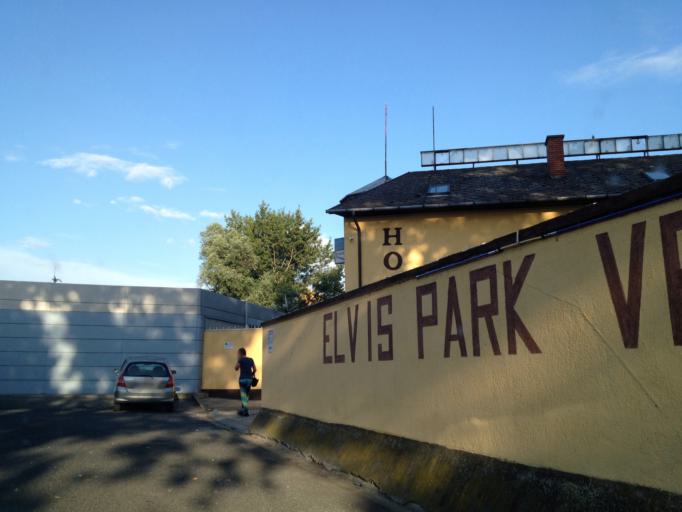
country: HU
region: Gyor-Moson-Sopron
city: Abda
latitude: 47.6836
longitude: 17.5686
